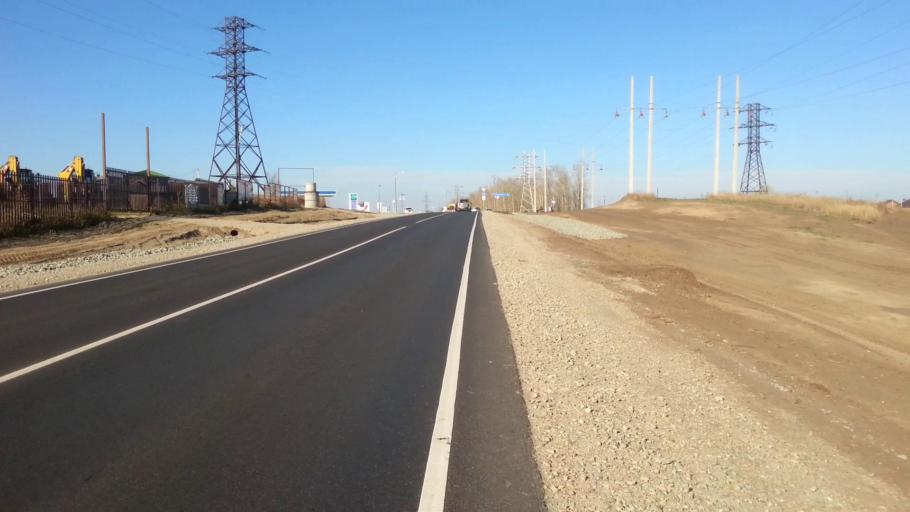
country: RU
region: Altai Krai
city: Sannikovo
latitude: 53.3352
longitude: 83.9384
